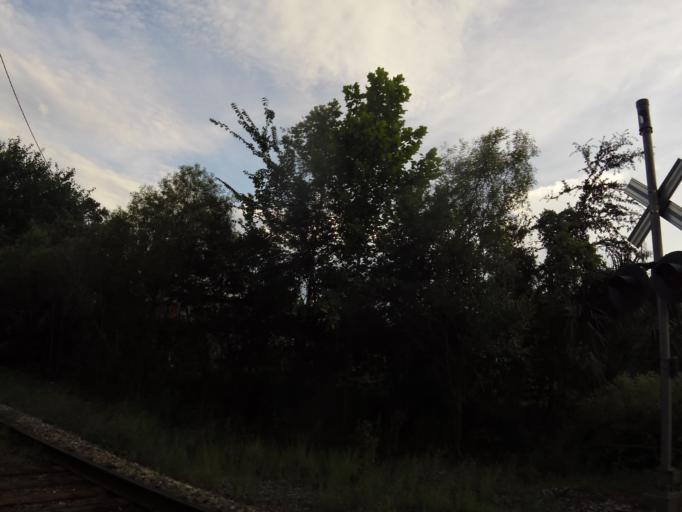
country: US
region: Florida
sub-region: Duval County
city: Jacksonville
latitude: 30.3242
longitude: -81.7661
